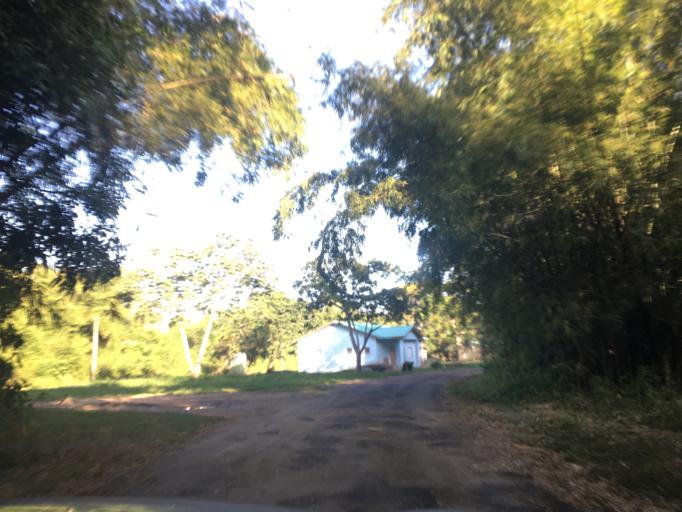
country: BZ
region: Stann Creek
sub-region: Dangriga
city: Dangriga
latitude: 16.8251
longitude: -88.3092
